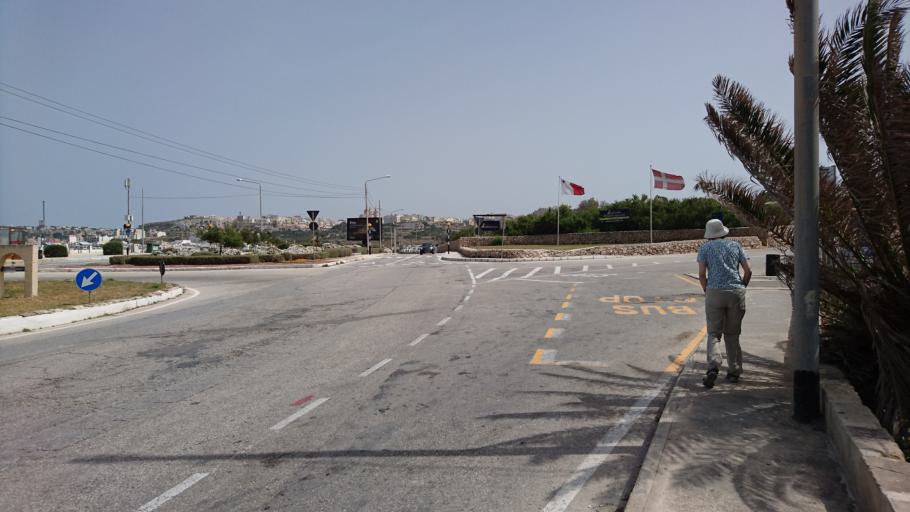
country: MT
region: Il-Mellieha
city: Mellieha
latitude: 35.9694
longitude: 14.3496
